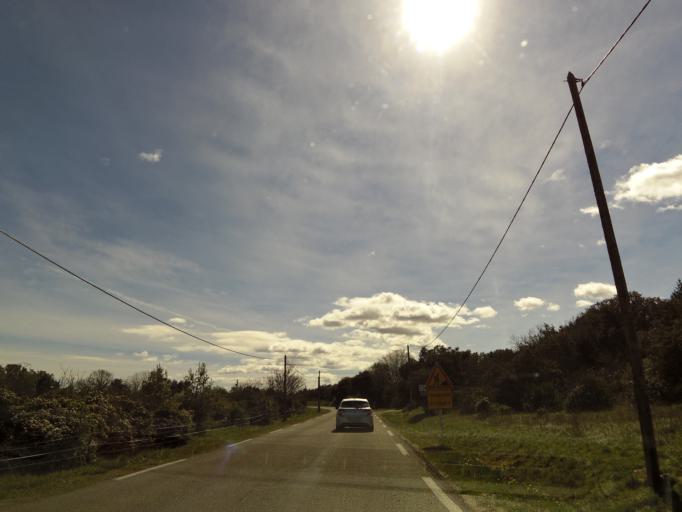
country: FR
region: Languedoc-Roussillon
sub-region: Departement du Gard
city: Bernis
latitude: 43.7769
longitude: 4.2823
